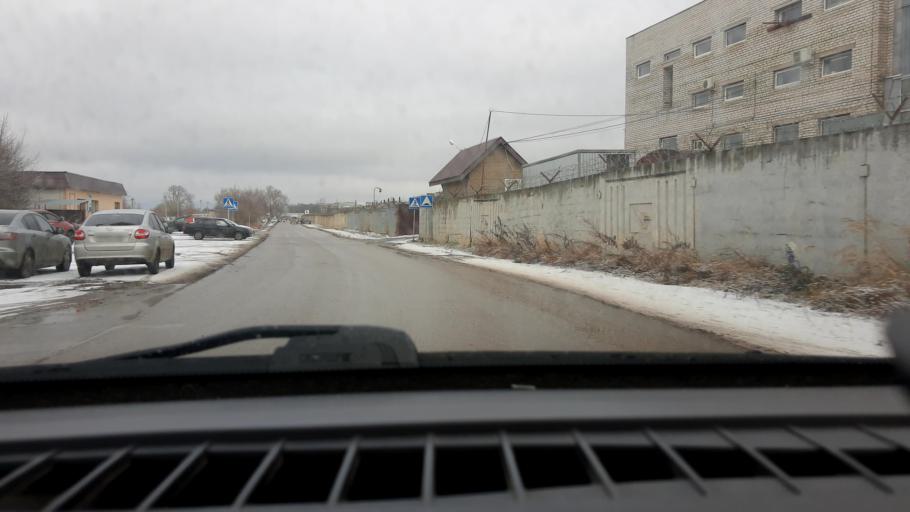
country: RU
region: Nizjnij Novgorod
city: Taremskoye
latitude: 55.9400
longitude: 43.0626
